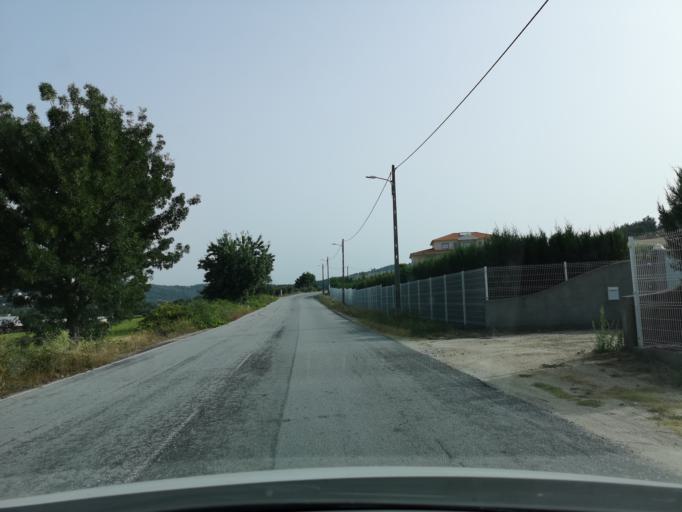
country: PT
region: Castelo Branco
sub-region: Belmonte
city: Belmonte
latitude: 40.3692
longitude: -7.3329
